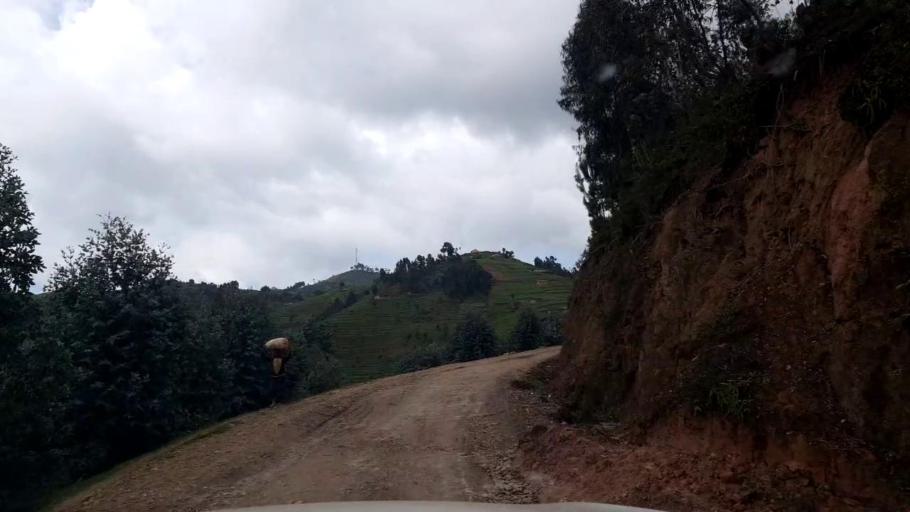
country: RW
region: Western Province
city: Kibuye
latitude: -1.9003
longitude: 29.4536
